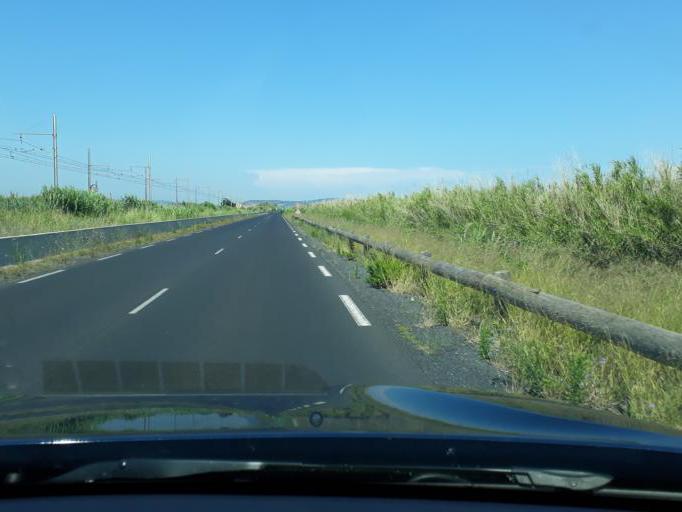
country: FR
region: Languedoc-Roussillon
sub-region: Departement de l'Herault
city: Marseillan
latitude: 43.3527
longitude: 3.5916
